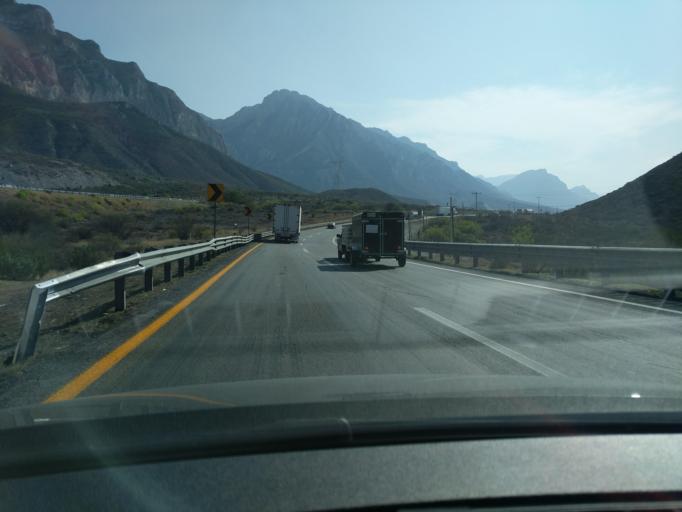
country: MX
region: Nuevo Leon
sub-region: Garcia
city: Las Torres de Guadalupe
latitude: 25.6844
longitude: -100.6601
